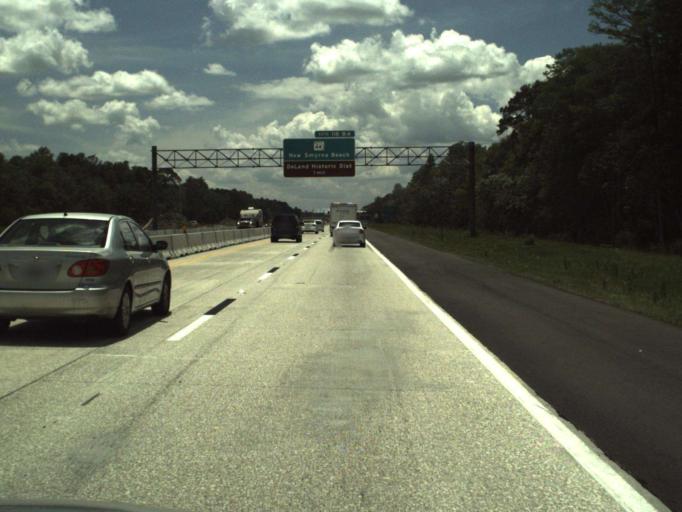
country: US
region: Florida
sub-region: Volusia County
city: Lake Helen
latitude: 29.0332
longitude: -81.2173
